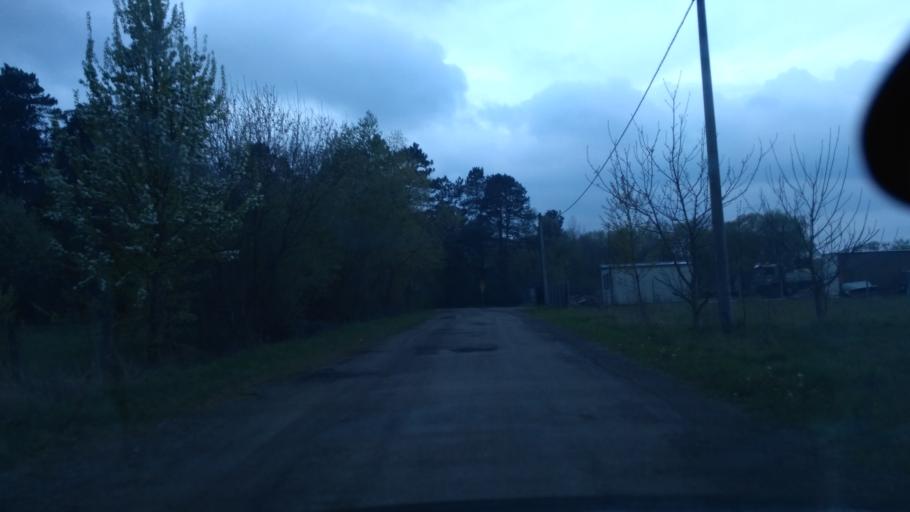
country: PL
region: Subcarpathian Voivodeship
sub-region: Powiat sanocki
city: Sanok
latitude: 49.5673
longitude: 22.2117
